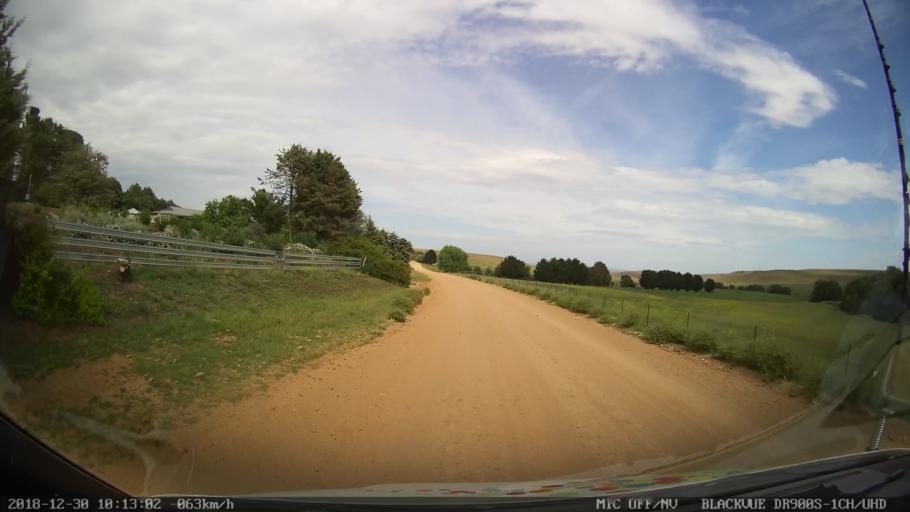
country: AU
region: New South Wales
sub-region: Snowy River
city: Berridale
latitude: -36.5381
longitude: 149.0701
